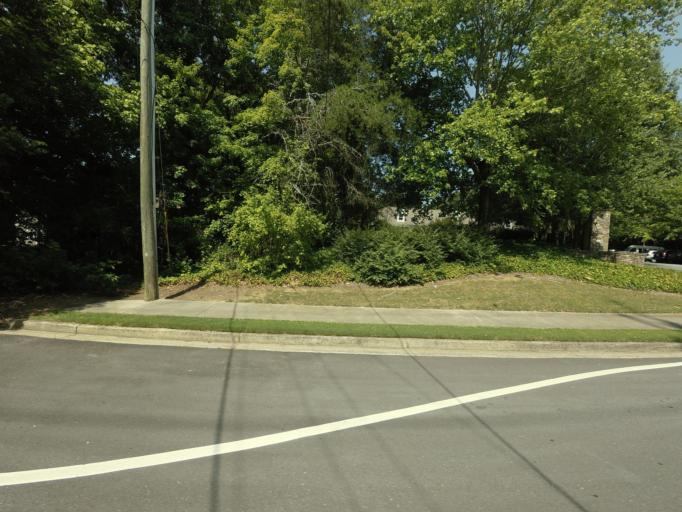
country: US
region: Georgia
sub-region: Fulton County
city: Alpharetta
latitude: 34.0026
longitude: -84.2765
